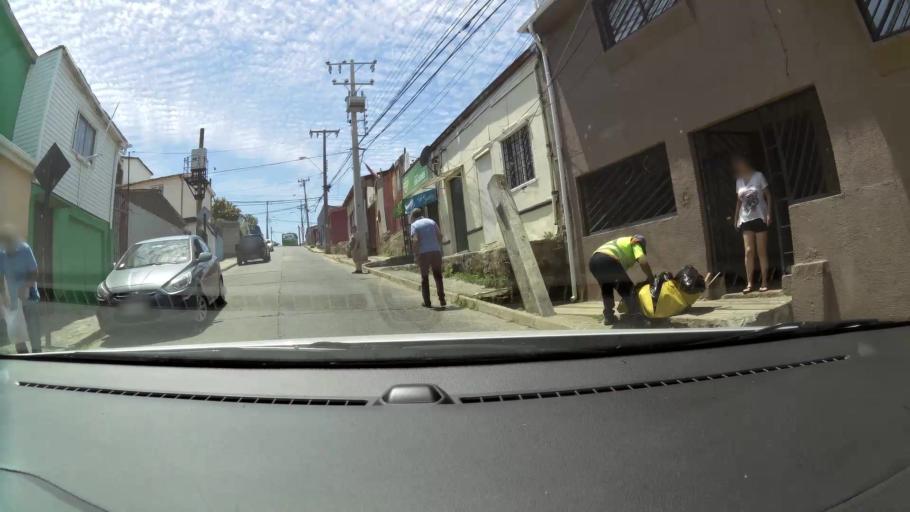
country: CL
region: Valparaiso
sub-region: Provincia de Valparaiso
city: Valparaiso
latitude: -33.0471
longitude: -71.5961
